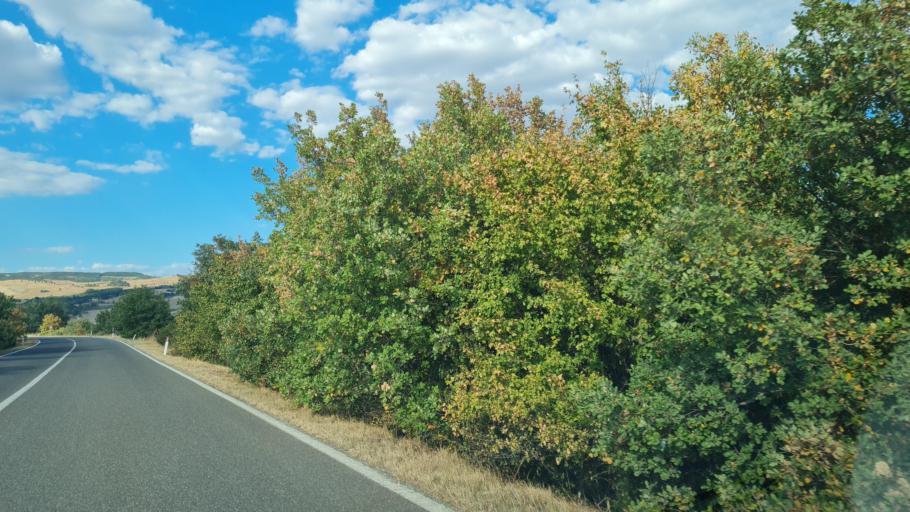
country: IT
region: Tuscany
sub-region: Provincia di Siena
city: Chianciano Terme
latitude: 43.0024
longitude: 11.7288
